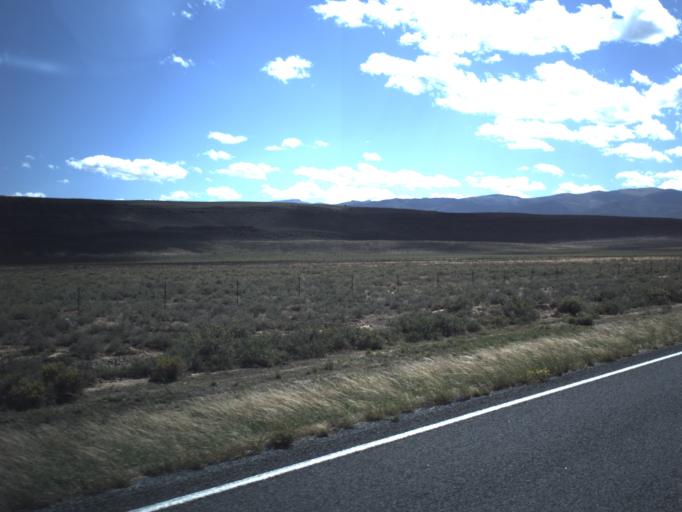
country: US
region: Utah
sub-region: Iron County
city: Enoch
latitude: 37.8729
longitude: -113.0316
